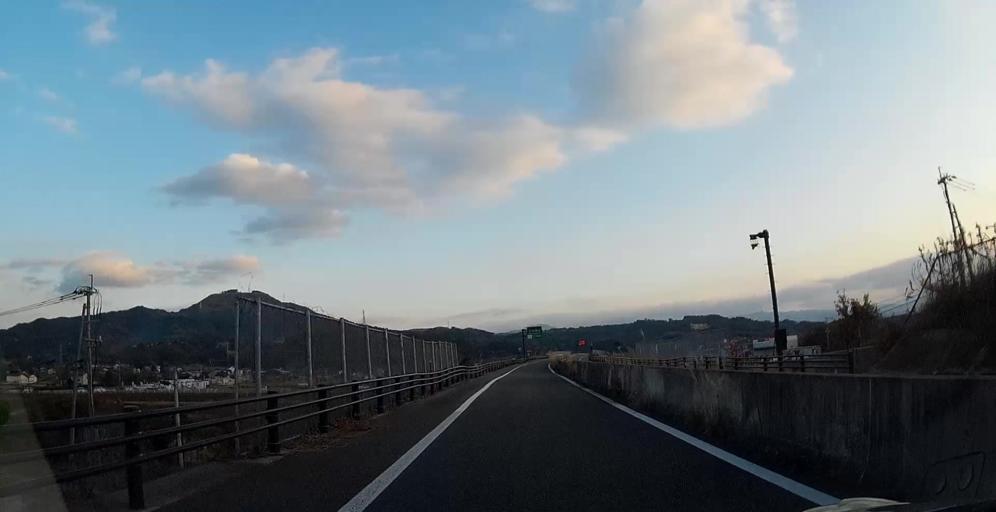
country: JP
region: Kumamoto
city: Kumamoto
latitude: 32.7504
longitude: 130.7984
